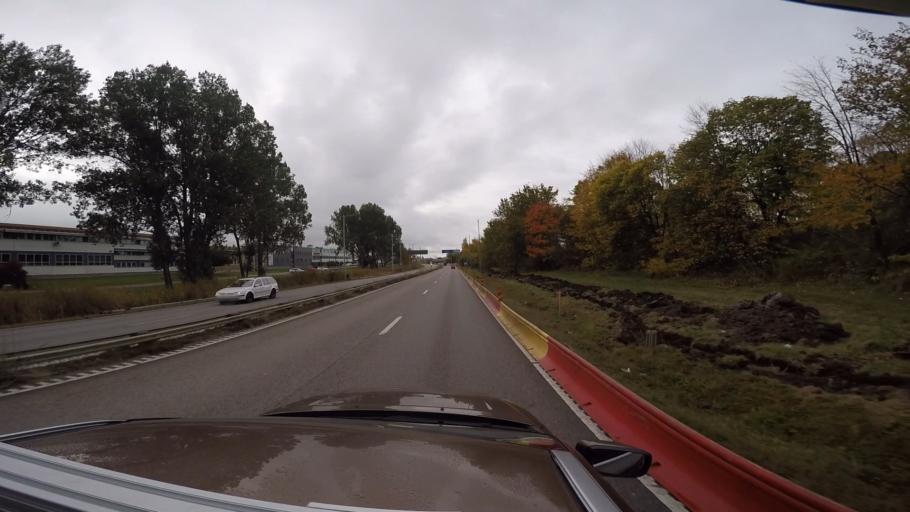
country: SE
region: Vaestra Goetaland
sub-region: Goteborg
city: Majorna
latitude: 57.6536
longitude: 11.9340
